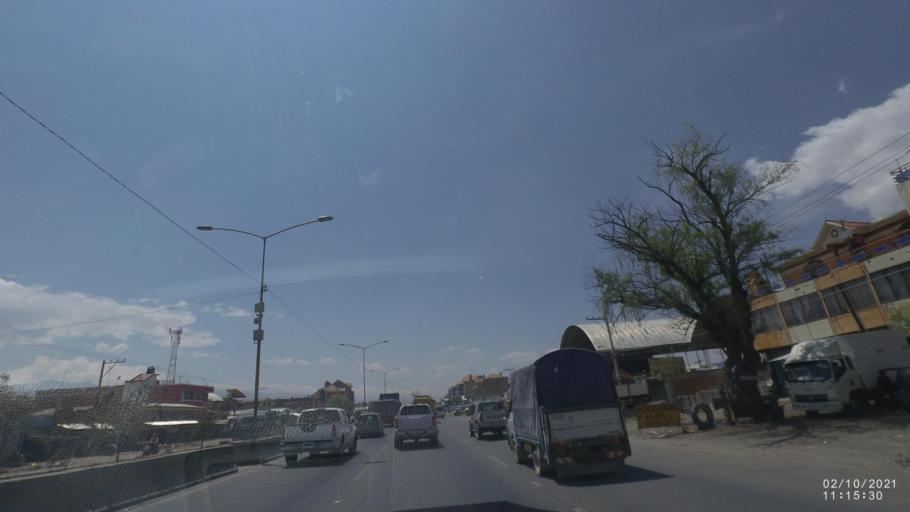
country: BO
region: Cochabamba
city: Sipe Sipe
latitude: -17.3954
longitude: -66.3040
